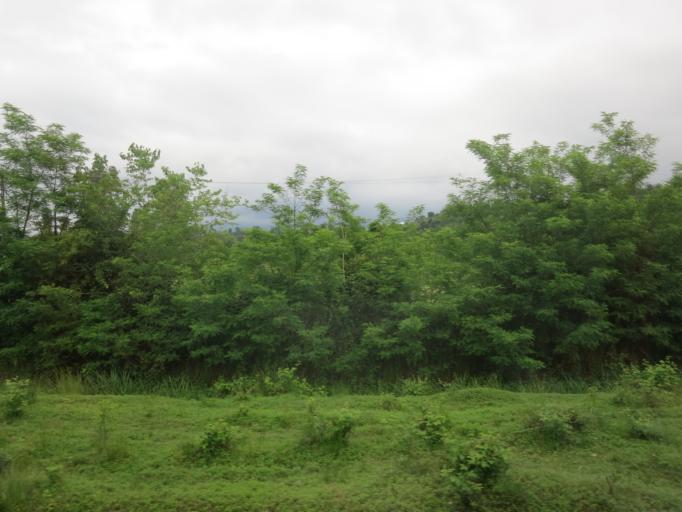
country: GE
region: Ajaria
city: Kobuleti
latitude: 41.7857
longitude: 41.7662
